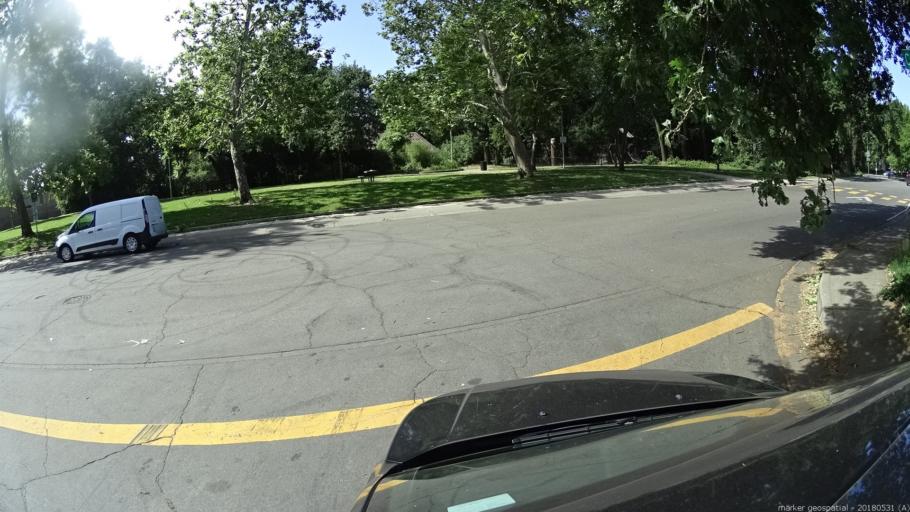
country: US
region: California
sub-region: Sacramento County
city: Sacramento
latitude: 38.6166
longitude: -121.5048
